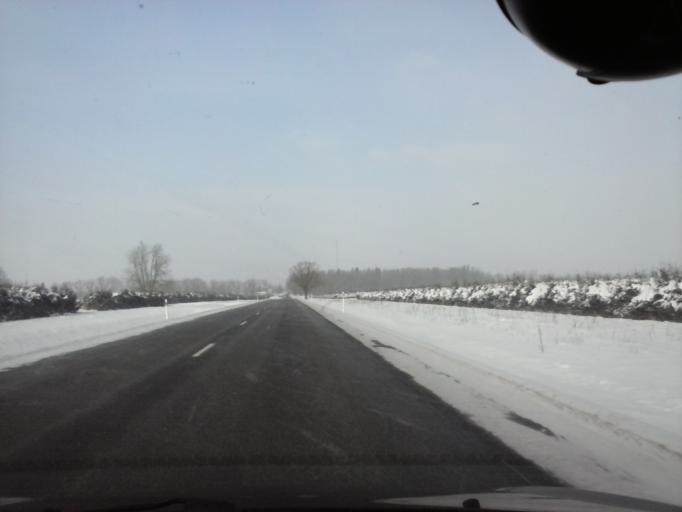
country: EE
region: Viljandimaa
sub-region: Abja vald
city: Abja-Paluoja
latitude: 58.3104
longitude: 25.3002
